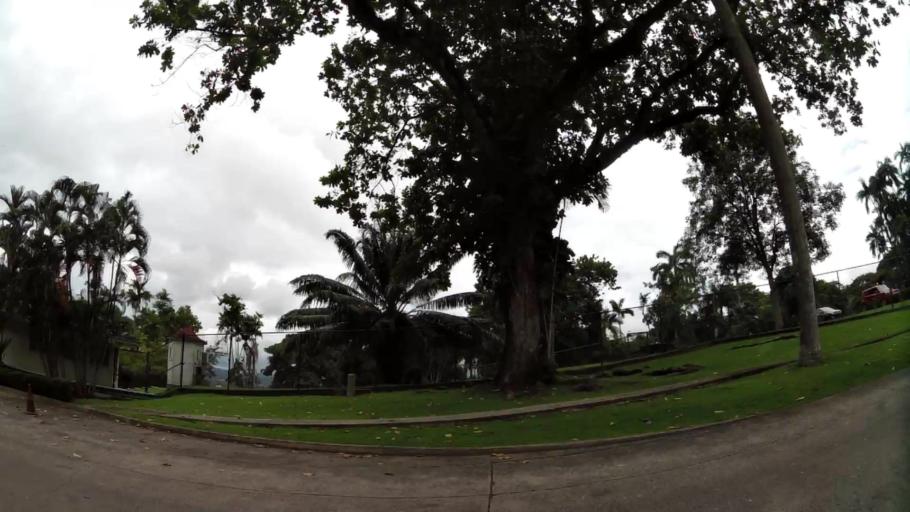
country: PA
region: Panama
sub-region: Distrito de Panama
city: Ancon
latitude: 8.9605
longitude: -79.5526
